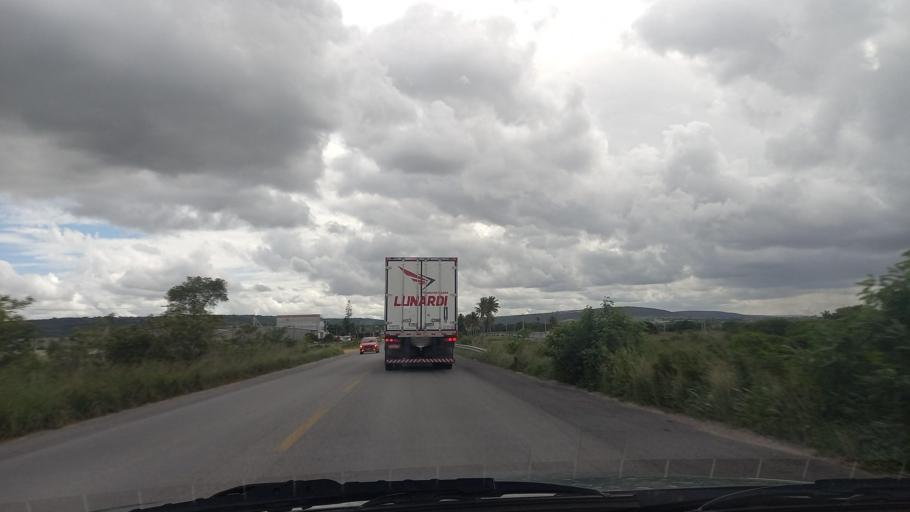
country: BR
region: Pernambuco
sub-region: Lajedo
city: Lajedo
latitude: -8.6628
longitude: -36.3501
